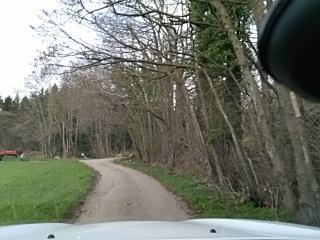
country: FR
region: Alsace
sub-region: Departement du Haut-Rhin
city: Orbey
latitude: 48.1257
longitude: 7.1395
